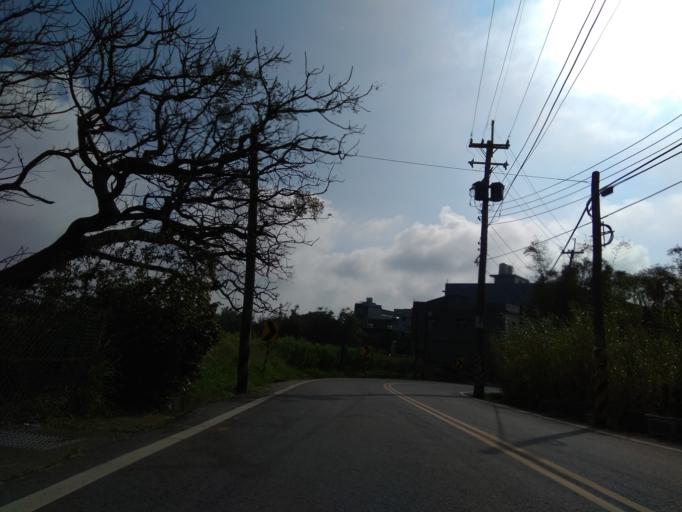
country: TW
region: Taiwan
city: Taoyuan City
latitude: 25.0760
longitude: 121.1696
